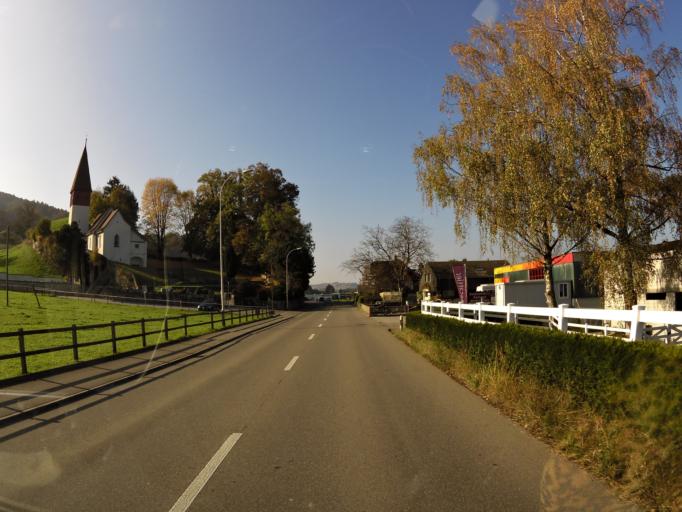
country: CH
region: Saint Gallen
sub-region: Wahlkreis Rheintal
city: Sankt Margrethen
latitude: 47.4556
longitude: 9.6234
